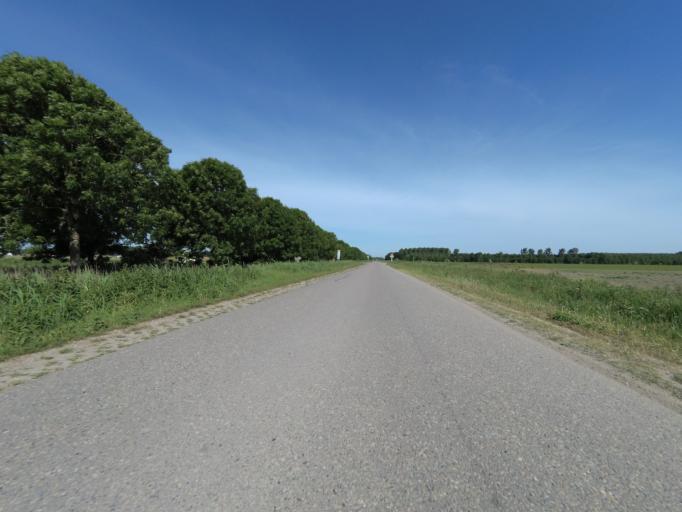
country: NL
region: Utrecht
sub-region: Gemeente Bunschoten
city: Spakenburg
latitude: 52.3263
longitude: 5.3347
